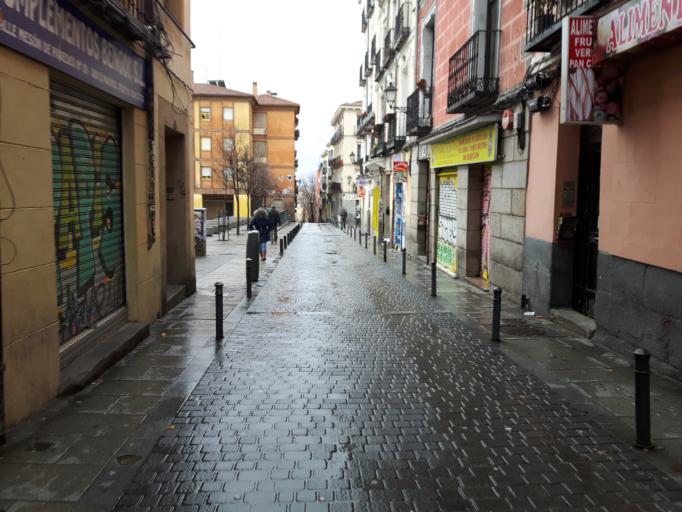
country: ES
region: Madrid
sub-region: Provincia de Madrid
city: Madrid
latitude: 40.4099
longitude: -3.7042
